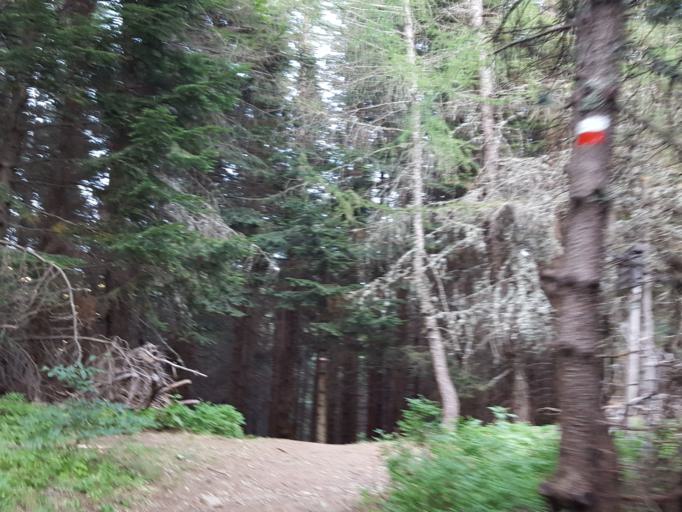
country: IT
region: Tuscany
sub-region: Provincia di Pistoia
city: Abetone
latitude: 44.1579
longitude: 10.6790
